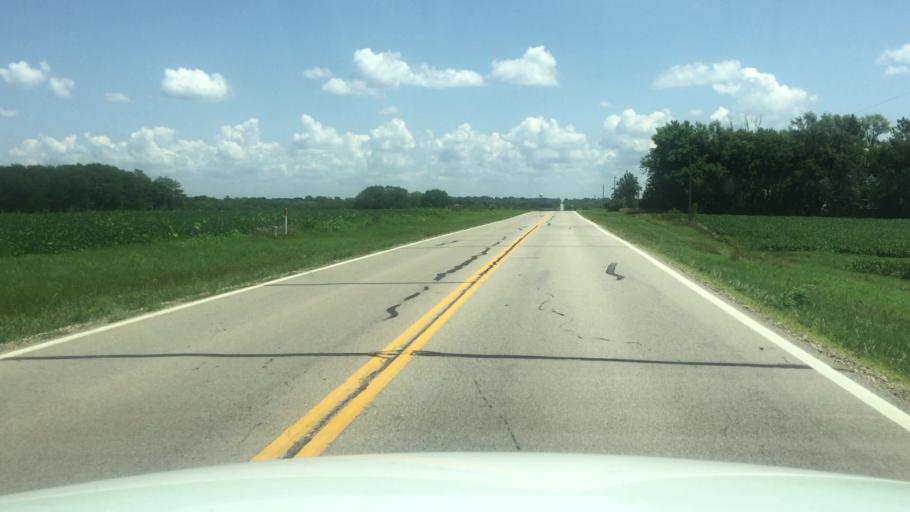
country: US
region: Kansas
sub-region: Brown County
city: Horton
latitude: 39.6674
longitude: -95.5668
